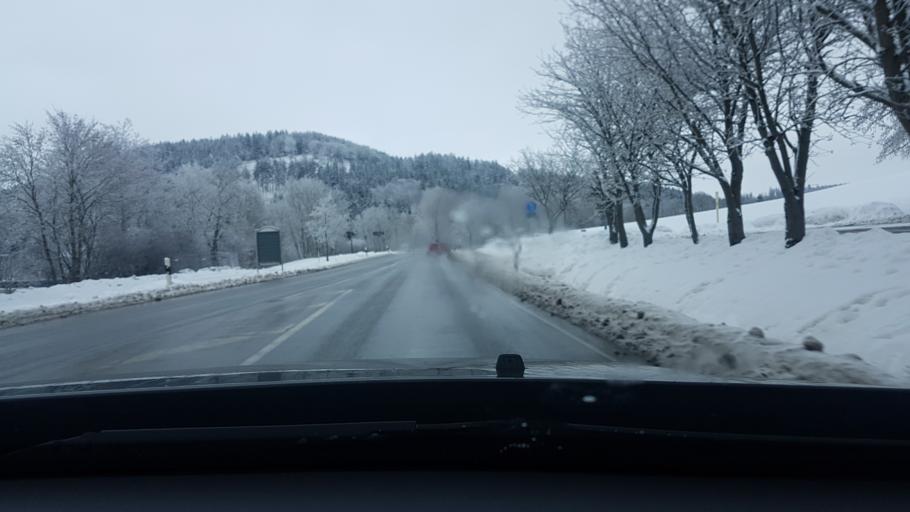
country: DE
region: Hesse
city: Willingen
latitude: 51.2819
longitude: 8.6297
